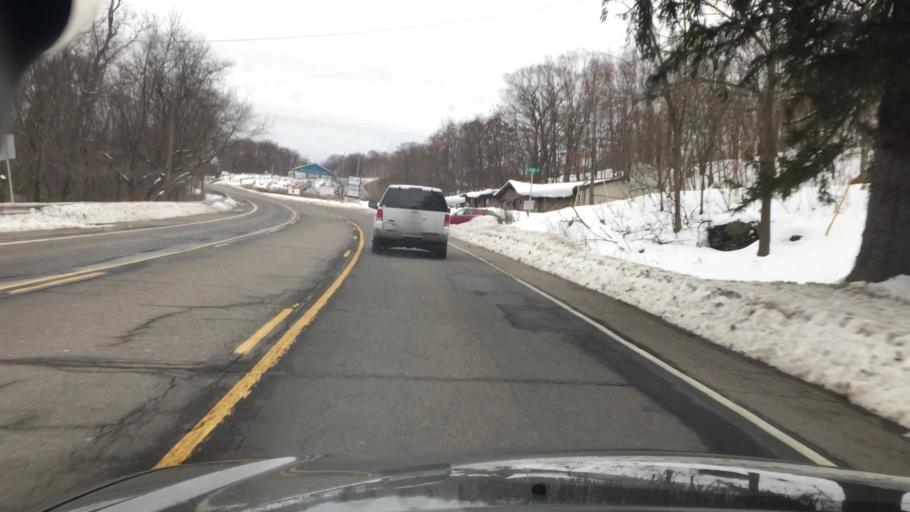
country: US
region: Pennsylvania
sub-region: Luzerne County
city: Mountain Top
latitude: 41.1723
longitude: -75.8790
